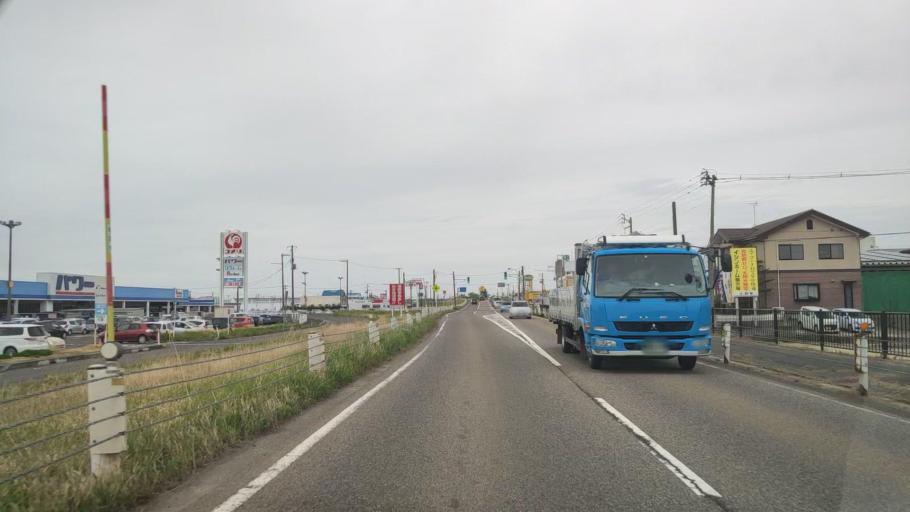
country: JP
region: Niigata
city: Niitsu-honcho
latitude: 37.7884
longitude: 139.1116
